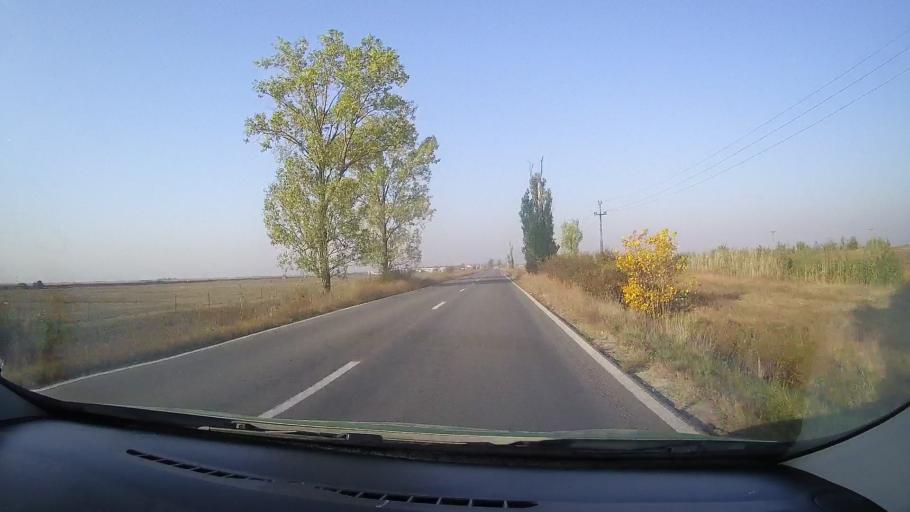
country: RO
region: Arad
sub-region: Comuna Socodor
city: Socodor
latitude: 46.5073
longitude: 21.4658
